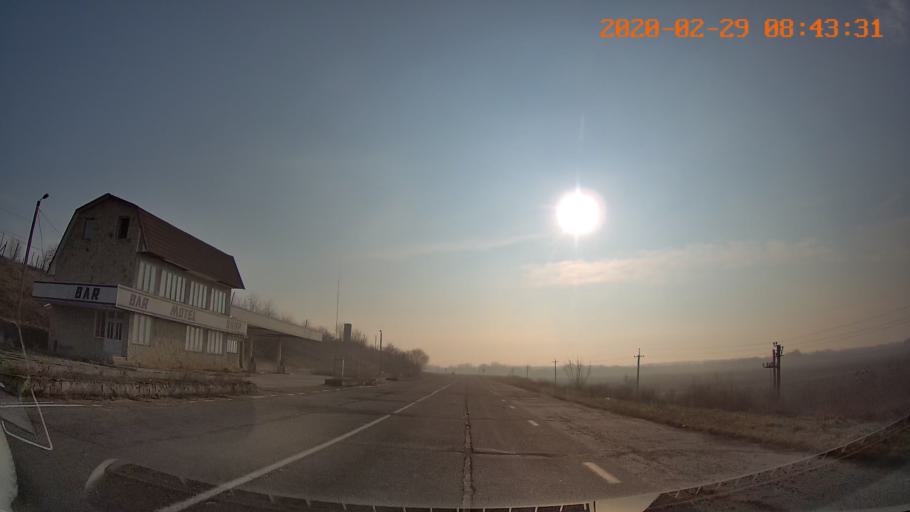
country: MD
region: Anenii Noi
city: Varnita
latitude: 46.9204
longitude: 29.4568
